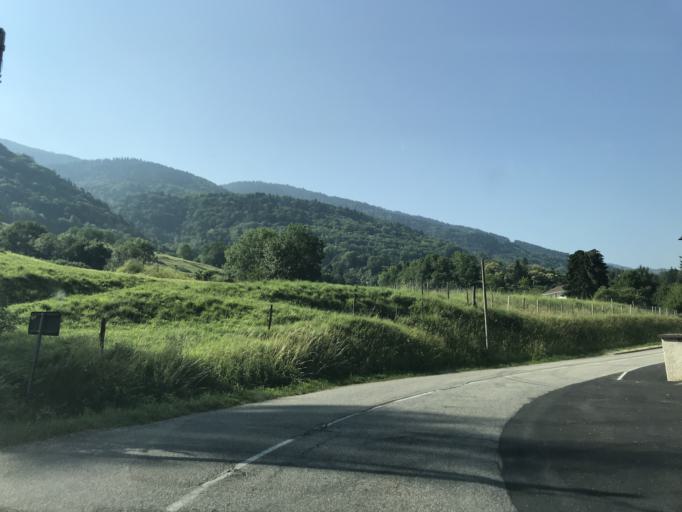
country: FR
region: Rhone-Alpes
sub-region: Departement de l'Isere
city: Allevard
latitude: 45.4248
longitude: 6.0978
